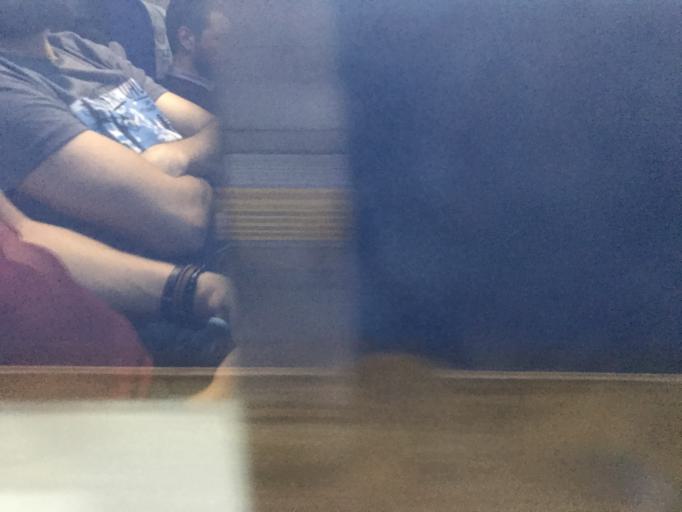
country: TR
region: Kocaeli
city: Hereke
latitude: 40.7764
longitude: 29.5955
